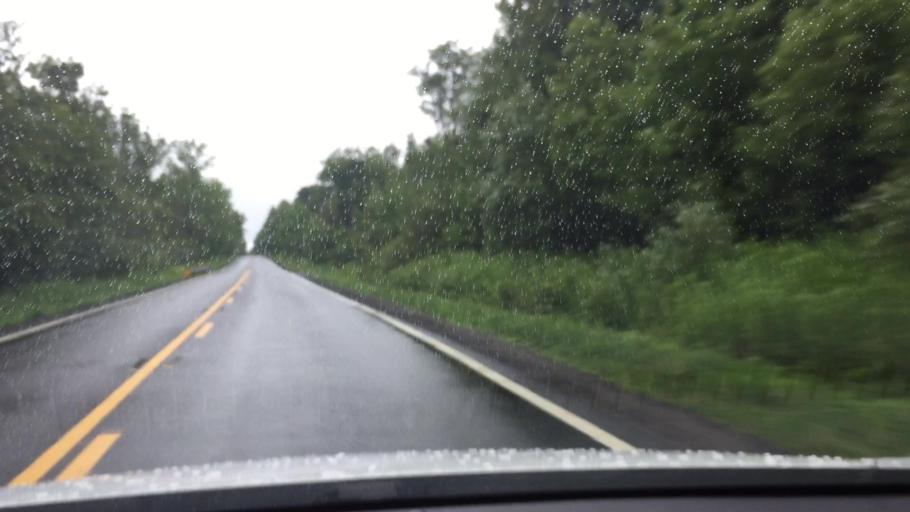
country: US
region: Massachusetts
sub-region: Berkshire County
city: Hinsdale
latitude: 42.3731
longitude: -73.1475
